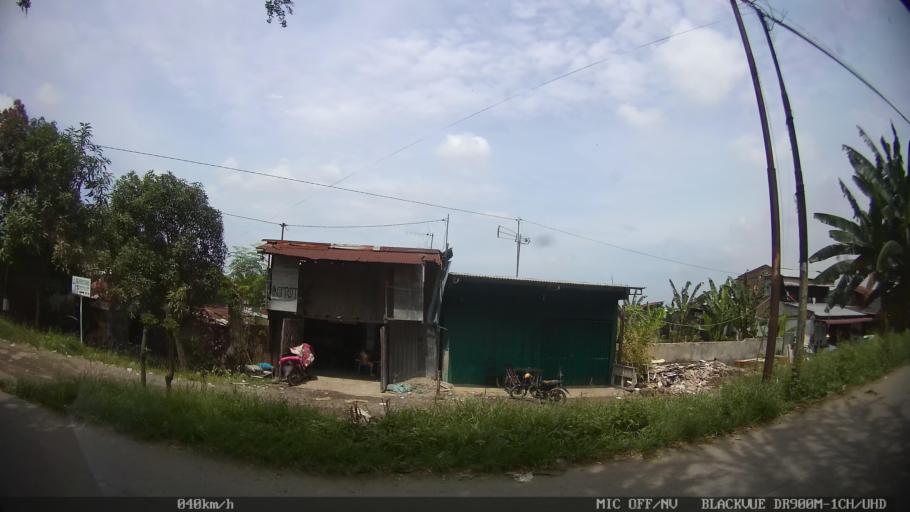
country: ID
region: North Sumatra
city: Medan
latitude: 3.6453
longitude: 98.6874
